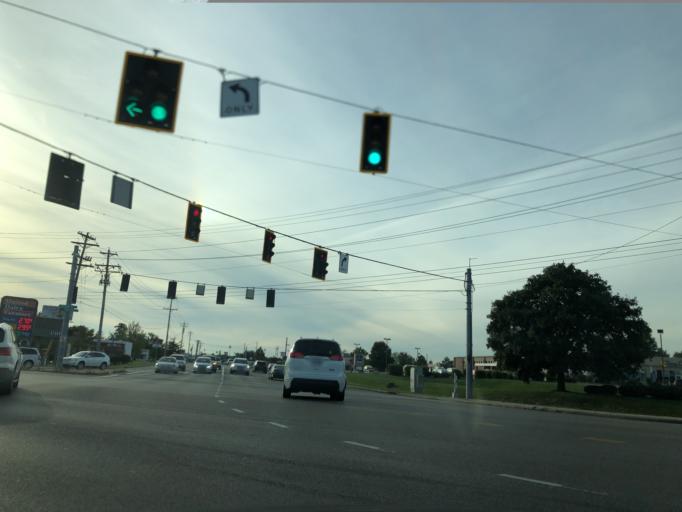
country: US
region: Ohio
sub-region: Warren County
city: Landen
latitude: 39.2907
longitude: -84.2984
